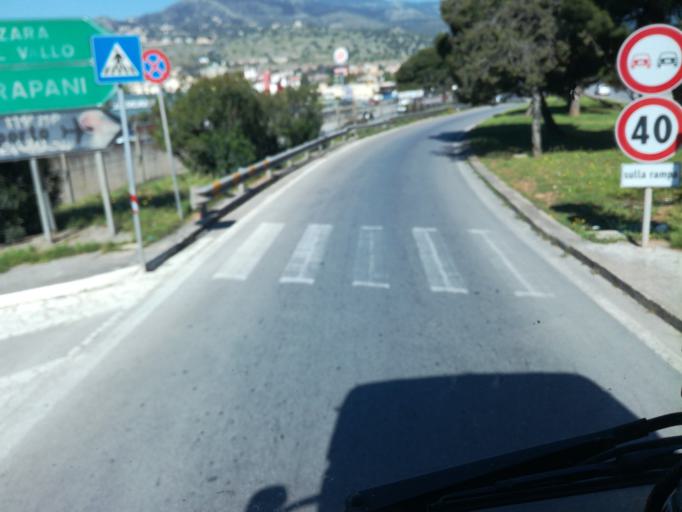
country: IT
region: Sicily
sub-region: Palermo
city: Palermo
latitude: 38.1497
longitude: 13.3262
